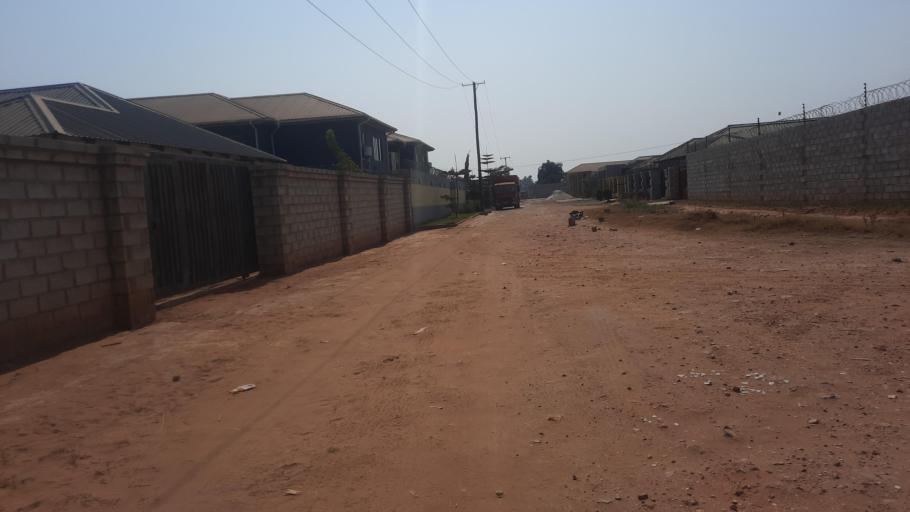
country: ZM
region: Lusaka
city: Lusaka
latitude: -15.3942
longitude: 28.3859
